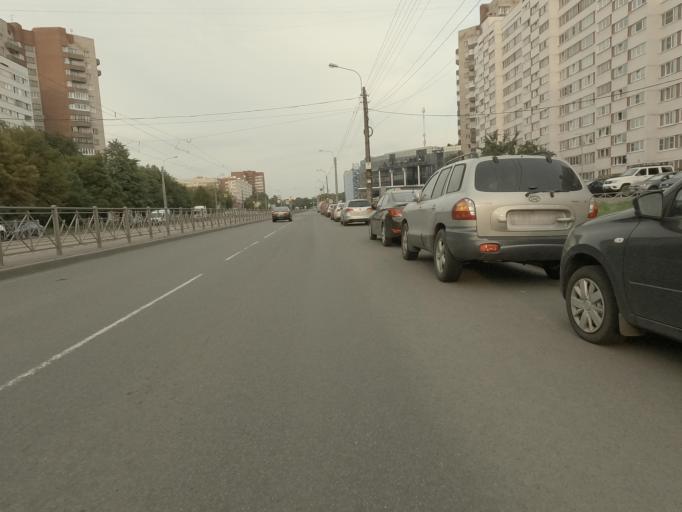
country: RU
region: St.-Petersburg
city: Dachnoye
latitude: 59.8595
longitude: 30.2438
